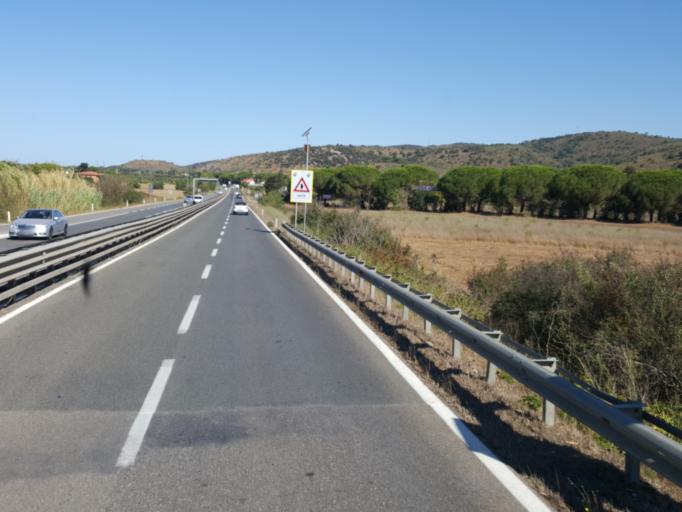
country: IT
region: Tuscany
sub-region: Provincia di Grosseto
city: Orbetello Scalo
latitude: 42.4310
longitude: 11.2847
